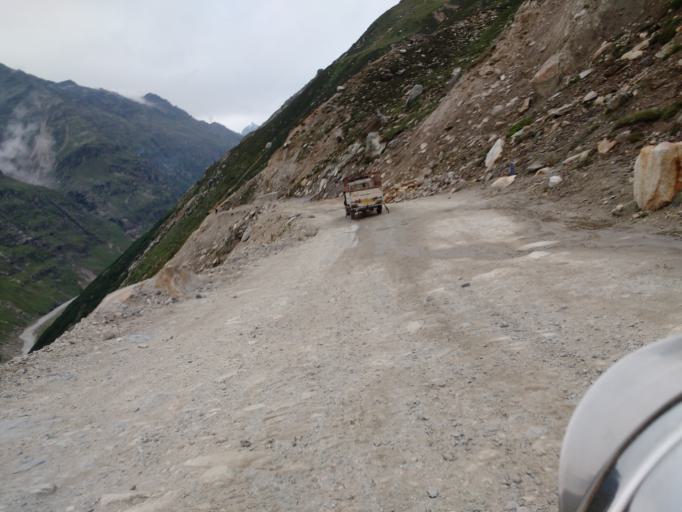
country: IN
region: Himachal Pradesh
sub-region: Kulu
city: Manali
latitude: 32.3792
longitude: 77.2661
